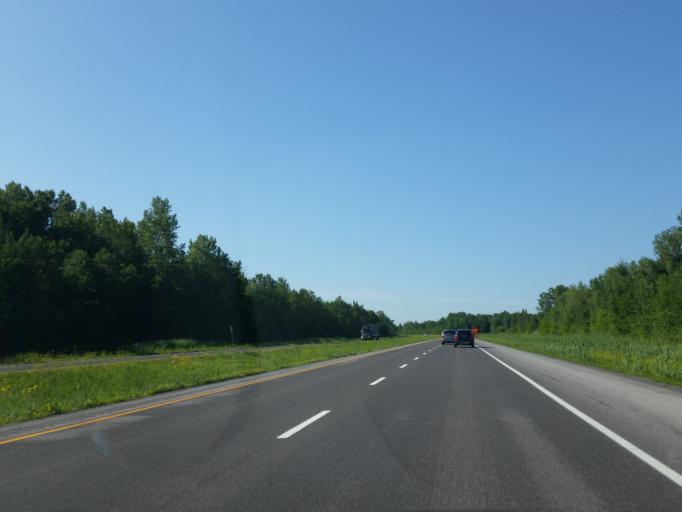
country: CA
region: Quebec
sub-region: Monteregie
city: Napierville
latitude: 45.2211
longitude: -73.4769
